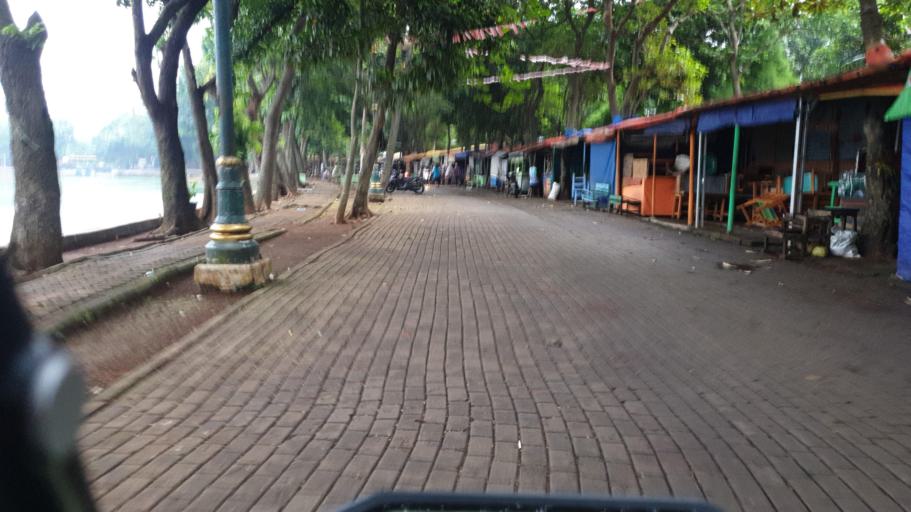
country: ID
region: West Java
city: Depok
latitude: -6.3402
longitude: 106.8269
